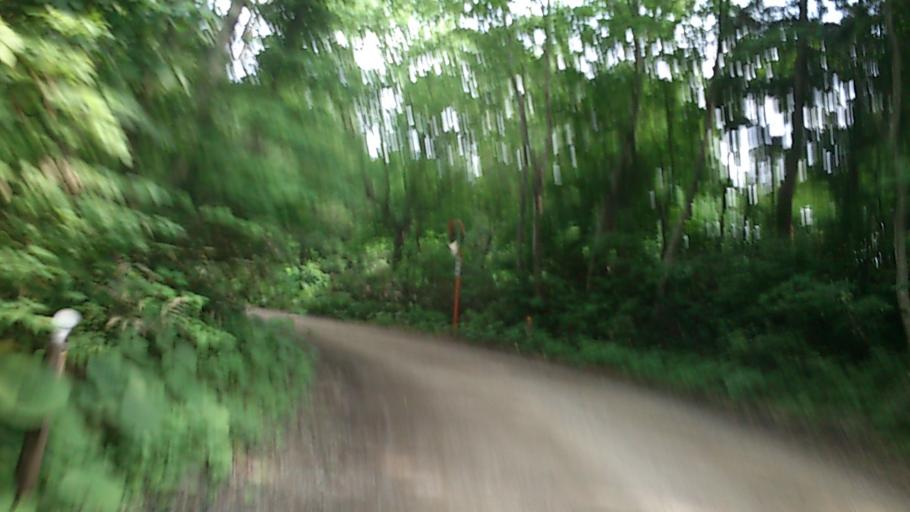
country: JP
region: Aomori
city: Hirosaki
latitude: 40.5617
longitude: 140.1793
